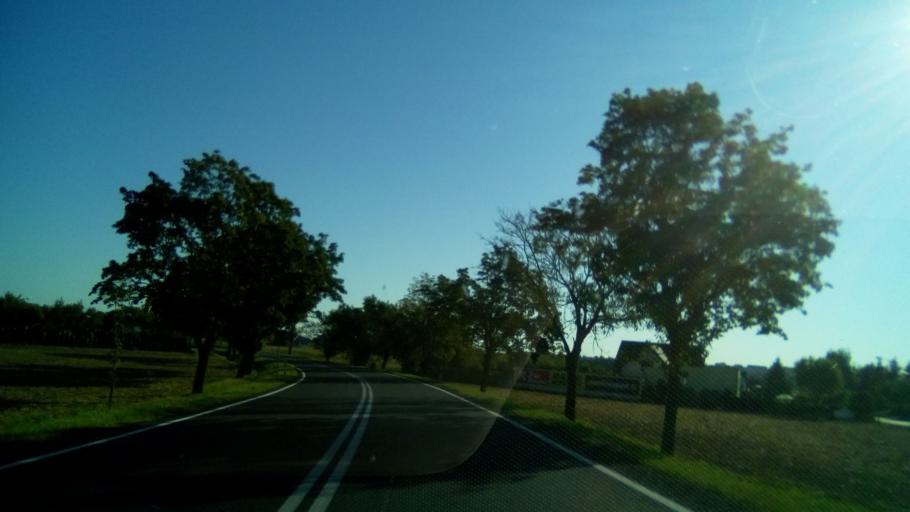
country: PL
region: Kujawsko-Pomorskie
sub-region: Powiat radziejowski
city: Radziejow
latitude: 52.6217
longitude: 18.5084
